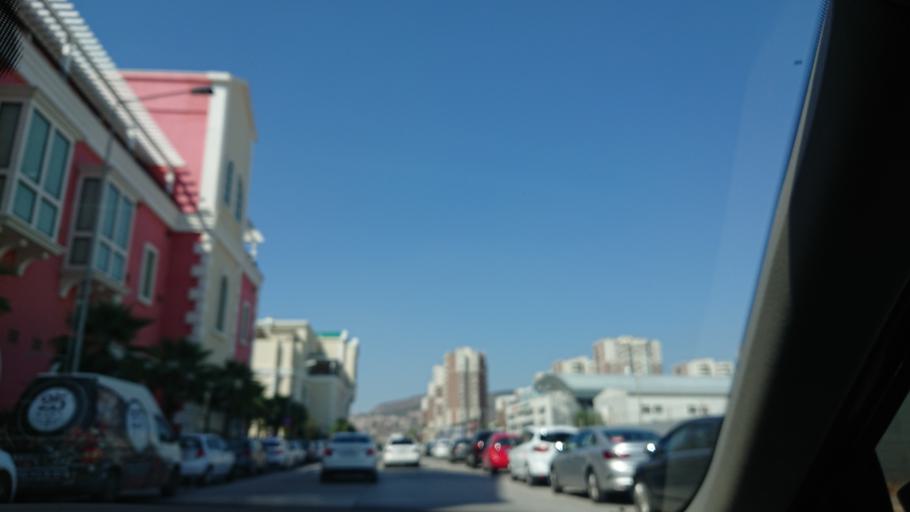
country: TR
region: Izmir
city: Karsiyaka
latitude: 38.4728
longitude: 27.0758
